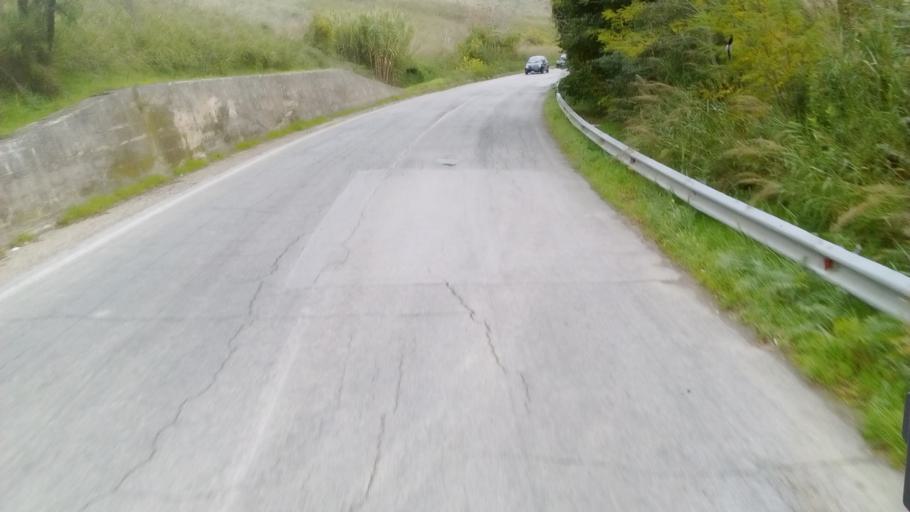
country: IT
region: Abruzzo
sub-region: Provincia di Chieti
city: San Salvo
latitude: 42.0584
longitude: 14.7201
